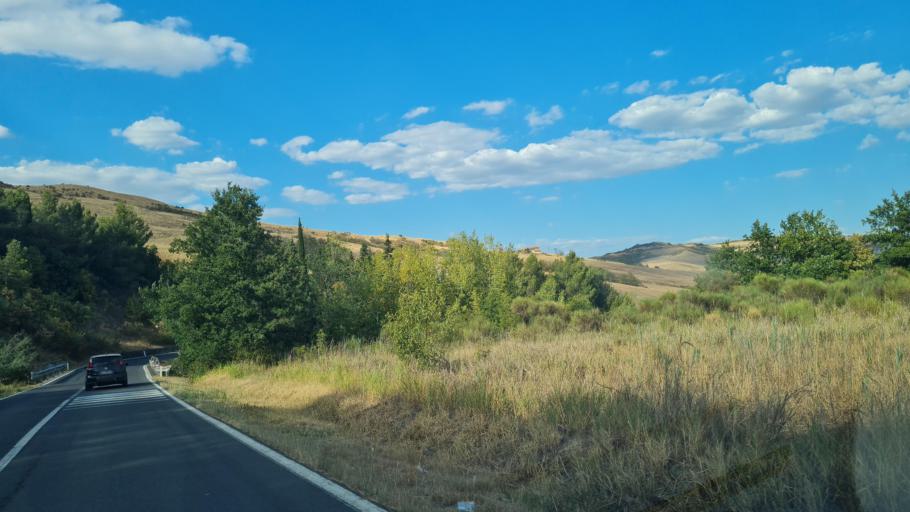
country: IT
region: Tuscany
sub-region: Provincia di Siena
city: Abbadia San Salvatore
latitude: 42.9344
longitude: 11.7014
